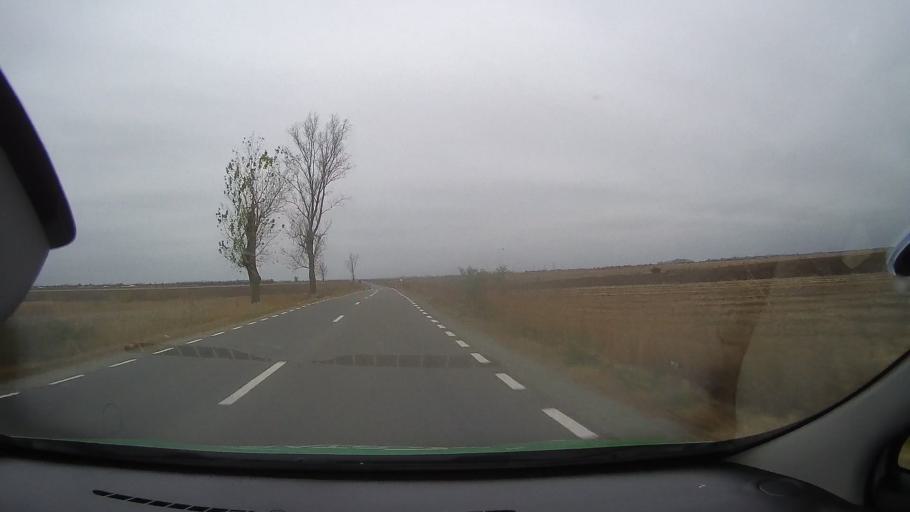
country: RO
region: Ialomita
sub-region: Comuna Gheorghe Lazar
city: Gheorghe Lazar
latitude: 44.6206
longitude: 27.3899
